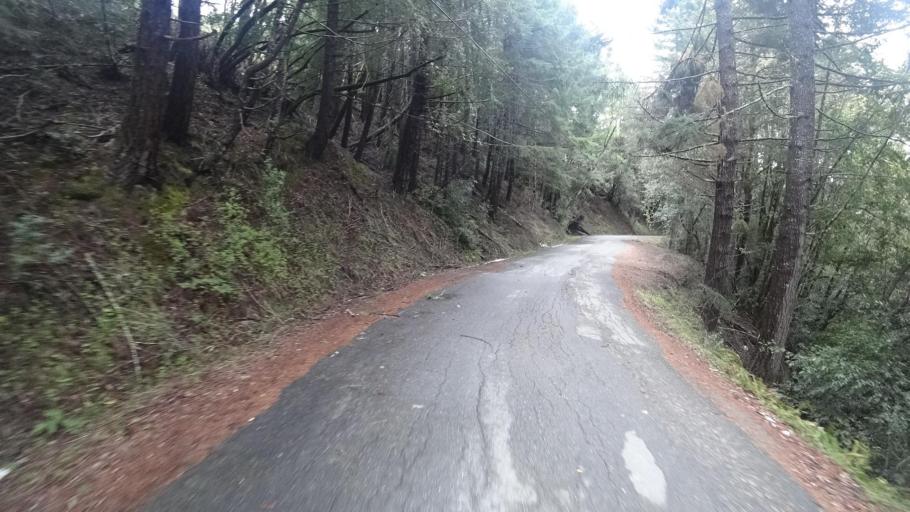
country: US
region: California
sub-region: Humboldt County
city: Blue Lake
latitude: 40.8791
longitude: -123.8809
